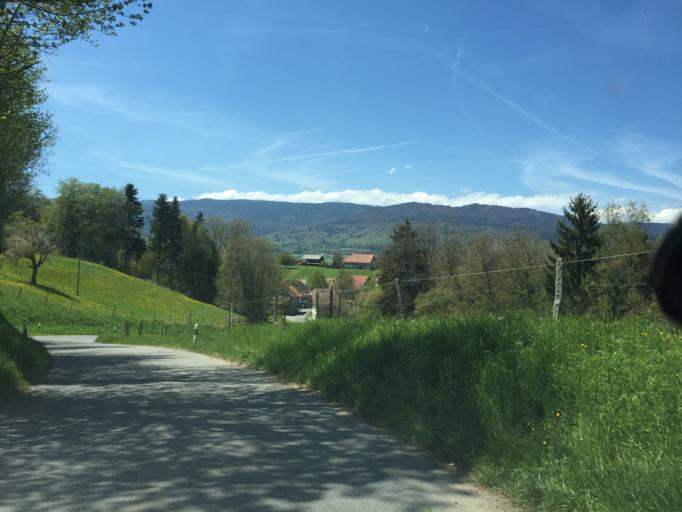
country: CH
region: Vaud
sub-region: Morges District
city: Mauraz
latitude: 46.6045
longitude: 6.4276
